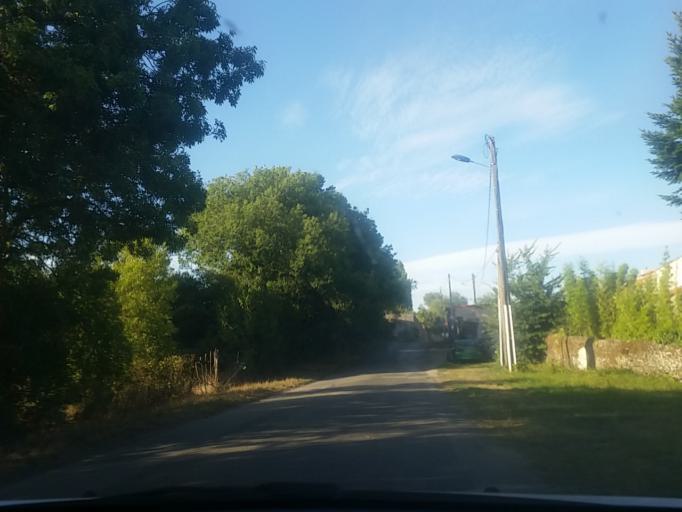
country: FR
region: Pays de la Loire
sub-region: Departement de la Loire-Atlantique
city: Bouguenais
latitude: 47.1854
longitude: -1.6353
